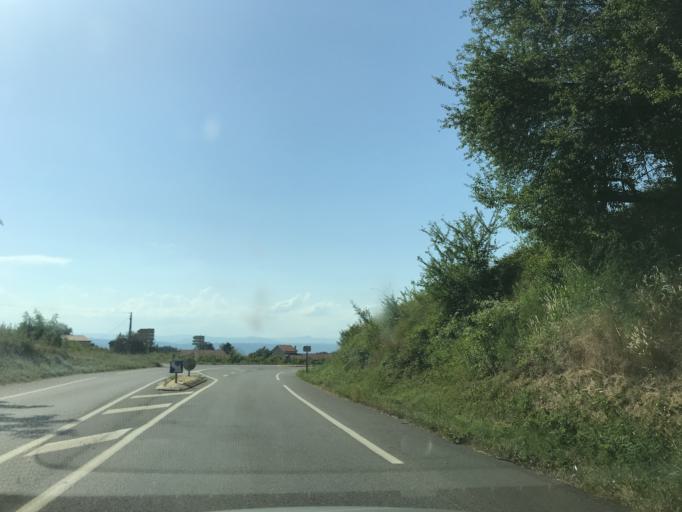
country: FR
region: Rhone-Alpes
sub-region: Departement de la Drome
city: Chateauneuf-sur-Isere
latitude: 45.0110
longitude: 4.9518
